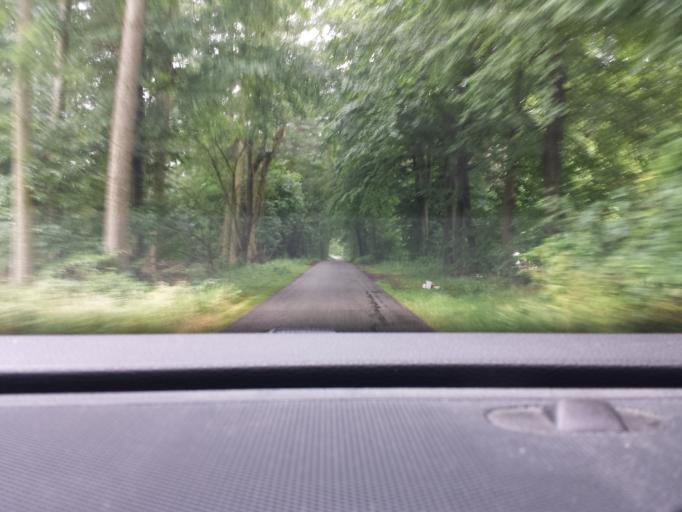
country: DE
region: North Rhine-Westphalia
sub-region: Regierungsbezirk Munster
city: Legden
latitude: 52.0687
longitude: 7.0659
